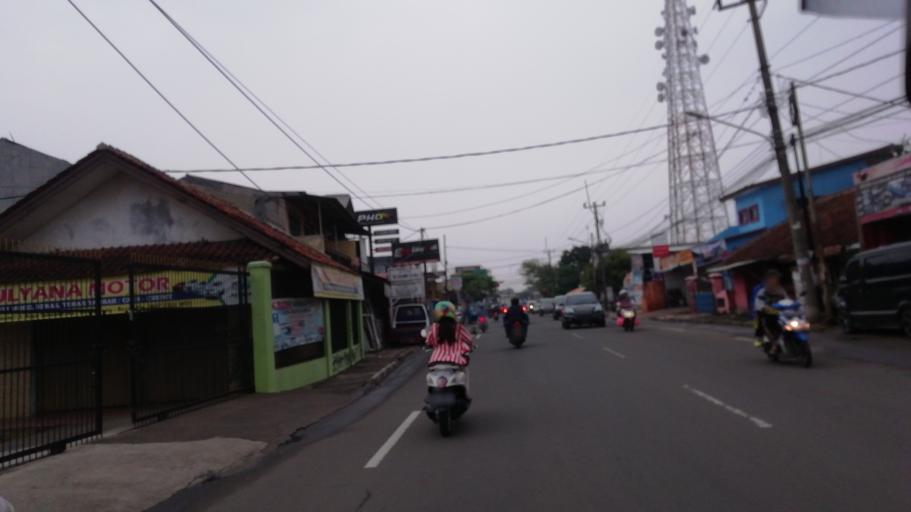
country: ID
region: West Java
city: Cibinong
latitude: -6.5033
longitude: 106.8083
